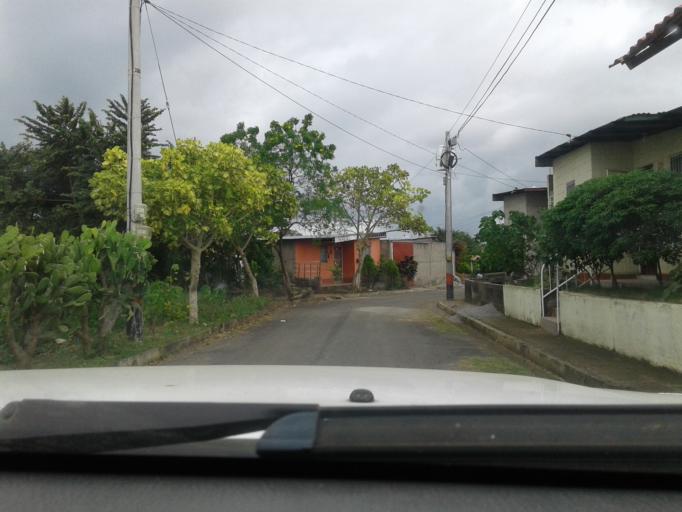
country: NI
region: Carazo
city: La Paz de Oriente
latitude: 11.8186
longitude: -86.1410
